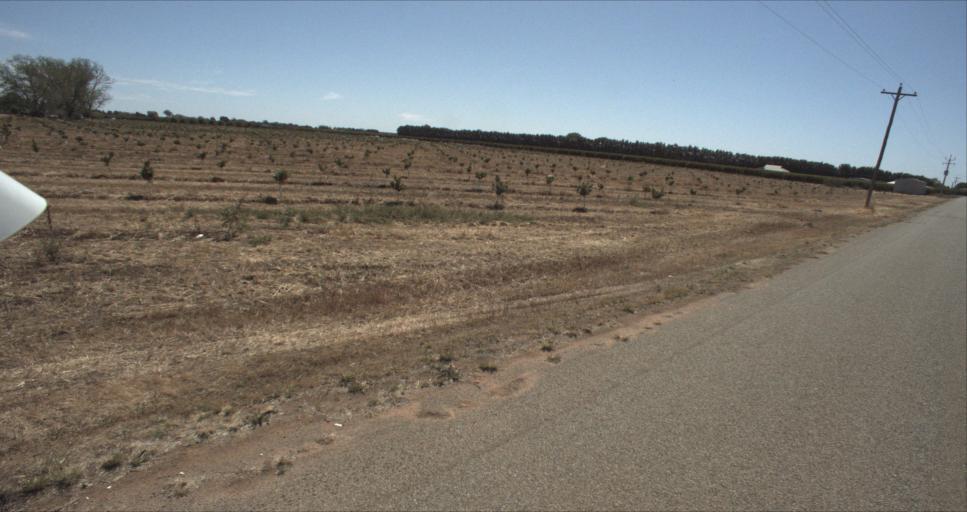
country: AU
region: New South Wales
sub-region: Leeton
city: Leeton
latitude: -34.5419
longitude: 146.3528
